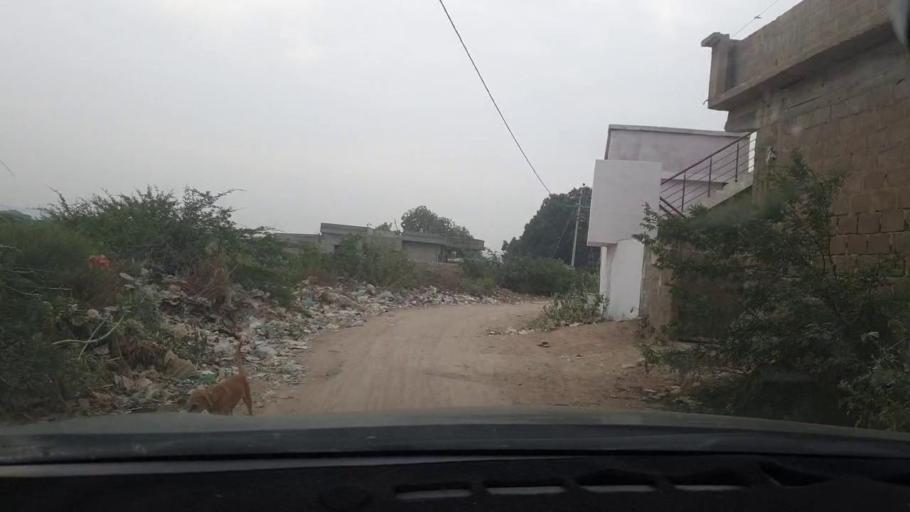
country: PK
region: Sindh
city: Malir Cantonment
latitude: 24.9222
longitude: 67.3185
